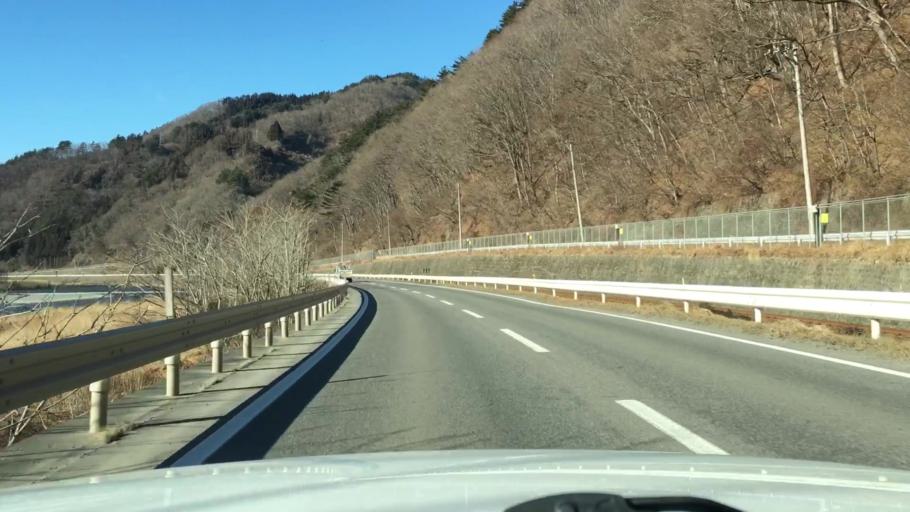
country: JP
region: Iwate
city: Miyako
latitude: 39.6321
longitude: 141.8530
